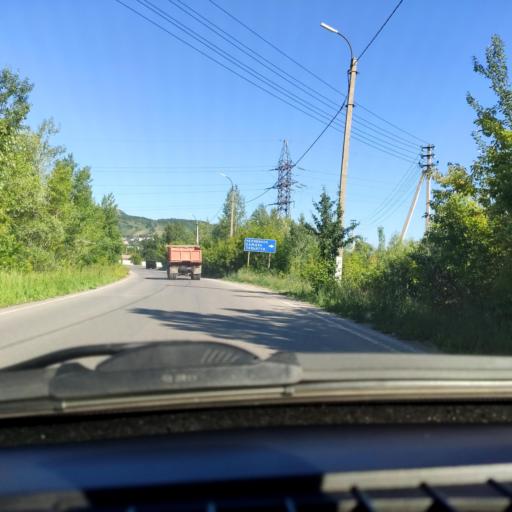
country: RU
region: Samara
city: Zhigulevsk
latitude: 53.4116
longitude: 49.4834
